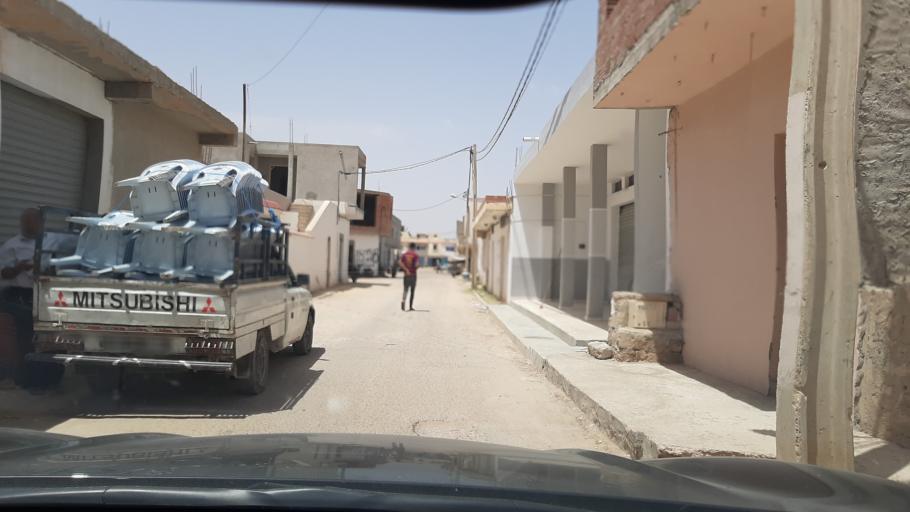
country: TN
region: Qabis
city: Gabes
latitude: 33.6189
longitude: 10.2908
